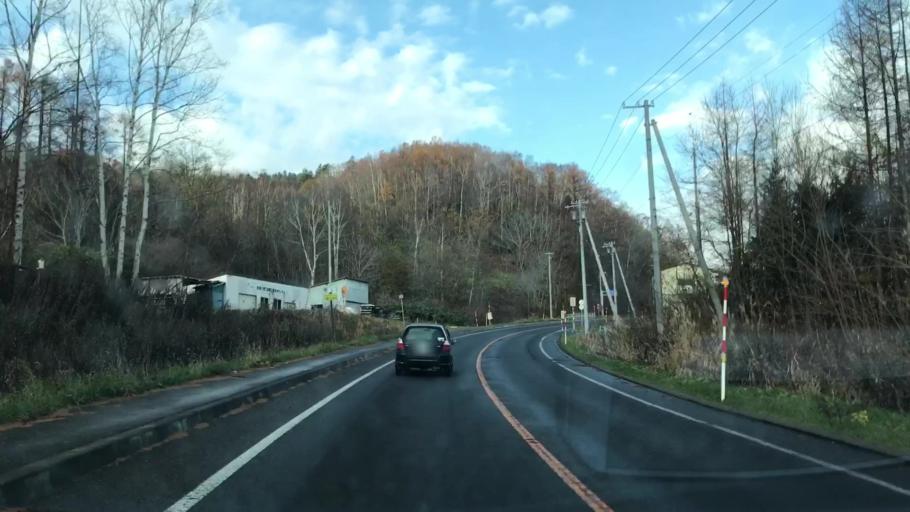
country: JP
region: Hokkaido
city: Yoichi
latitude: 43.2113
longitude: 140.7506
